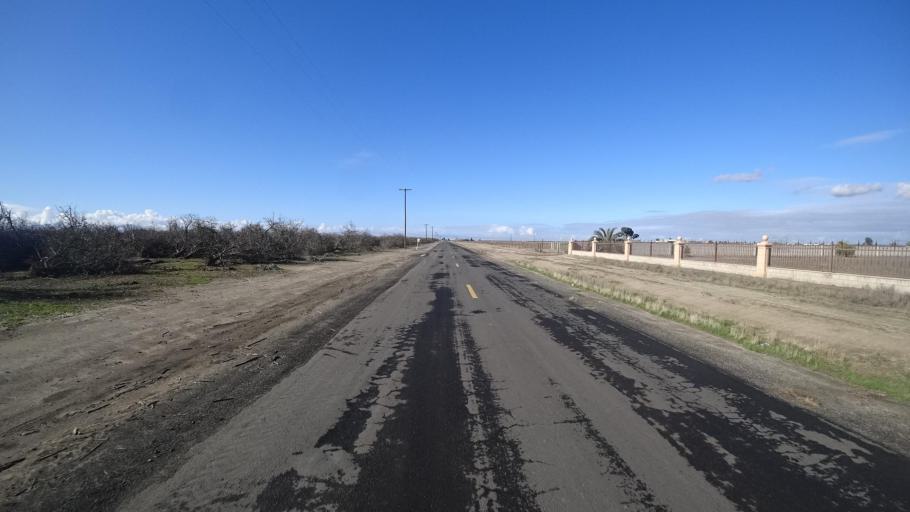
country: US
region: California
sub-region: Kern County
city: Rosedale
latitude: 35.3689
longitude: -119.2295
